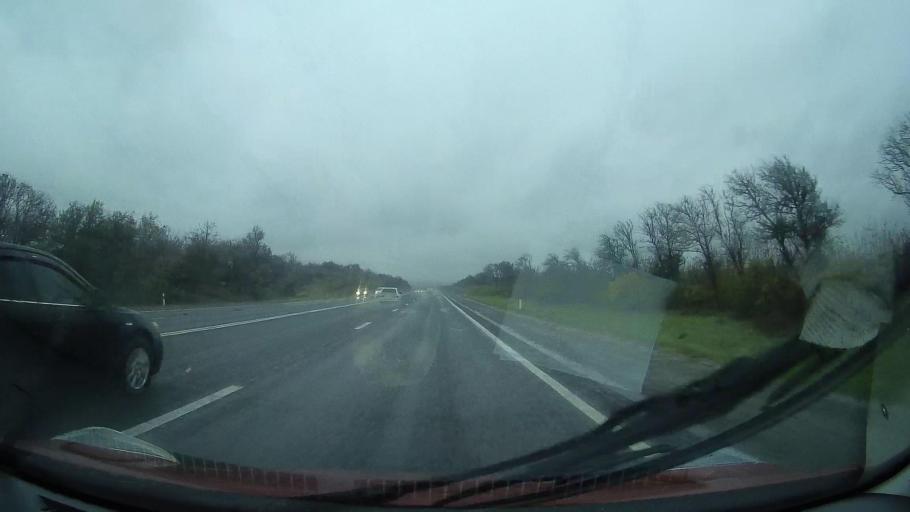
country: RU
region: Stavropol'skiy
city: Nevinnomyssk
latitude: 44.6176
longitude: 42.1003
